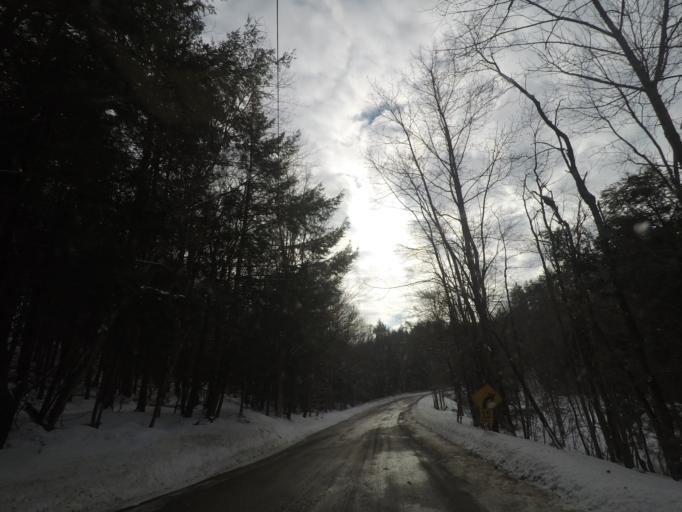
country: US
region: New York
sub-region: Rensselaer County
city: Averill Park
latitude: 42.6355
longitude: -73.4808
